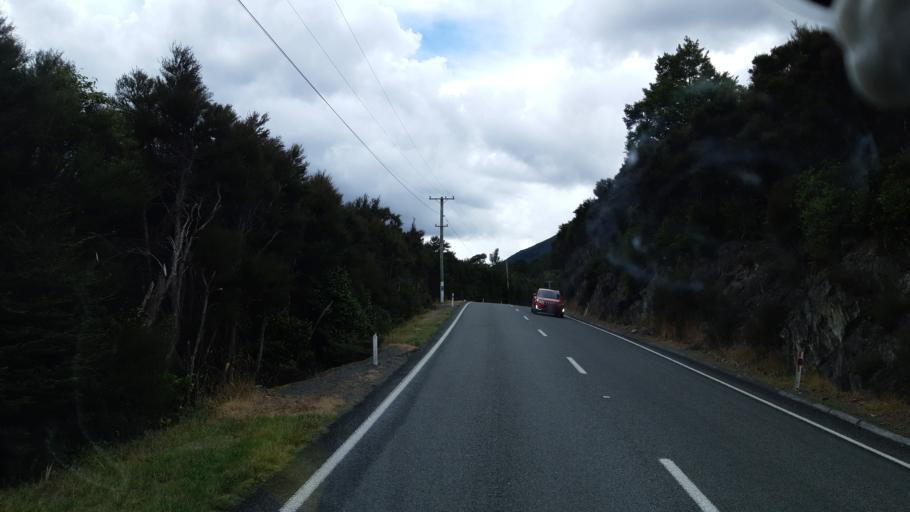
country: NZ
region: Canterbury
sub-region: Hurunui District
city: Amberley
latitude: -42.5468
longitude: 172.3504
